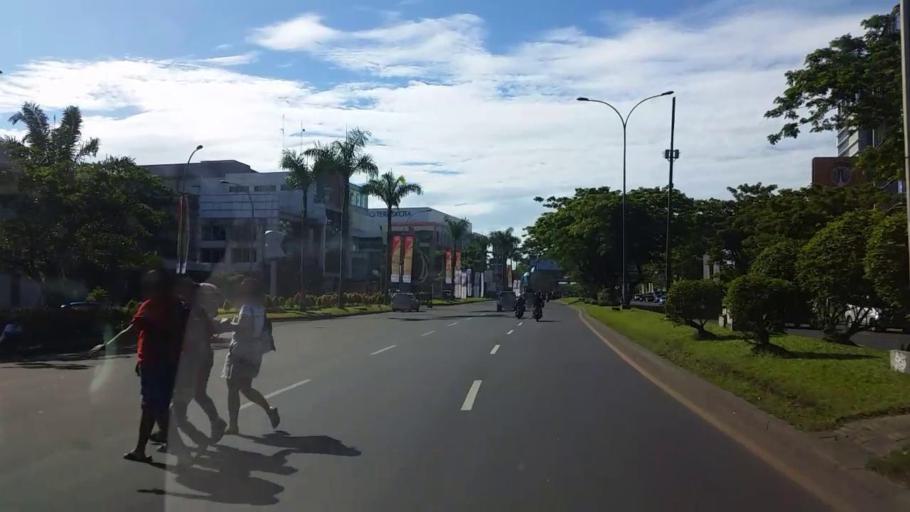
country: ID
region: West Java
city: Serpong
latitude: -6.2931
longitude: 106.6661
